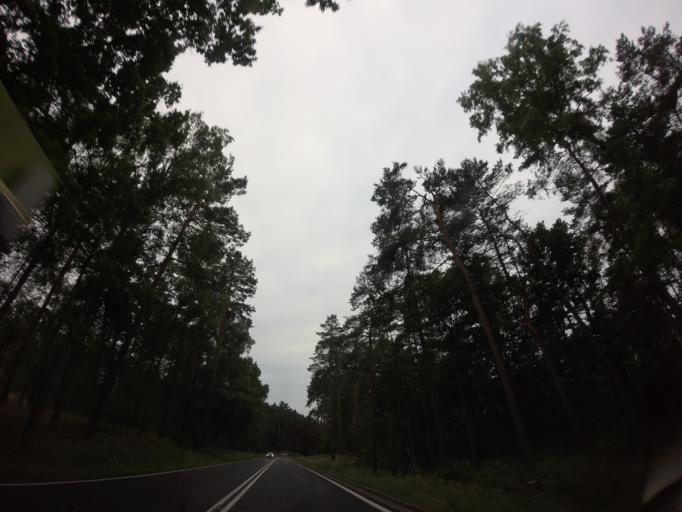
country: PL
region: West Pomeranian Voivodeship
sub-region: Powiat drawski
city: Kalisz Pomorski
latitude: 53.2925
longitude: 15.9554
